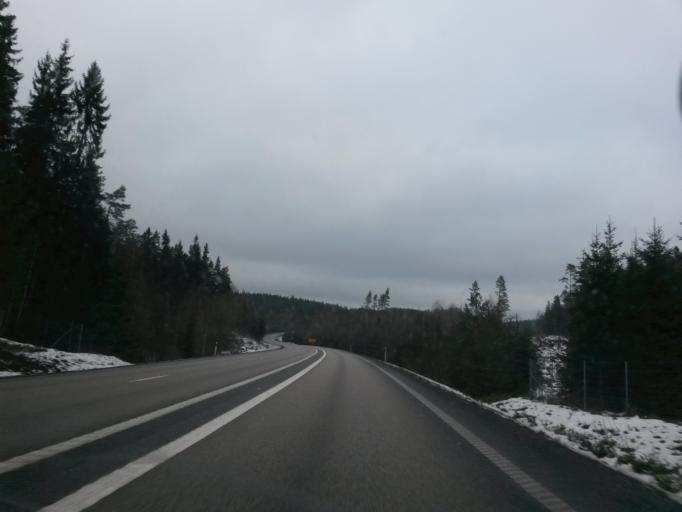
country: SE
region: Vaestra Goetaland
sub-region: Marks Kommun
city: Fritsla
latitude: 57.5646
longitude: 12.8338
